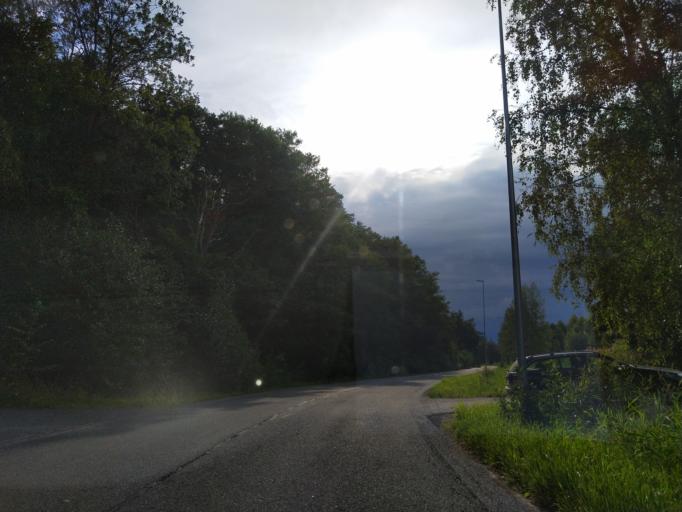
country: FI
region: Varsinais-Suomi
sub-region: Turku
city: Turku
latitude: 60.4278
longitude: 22.2133
